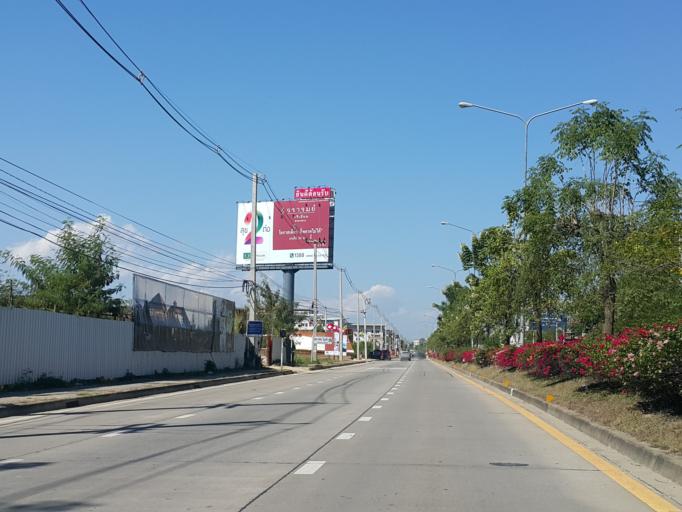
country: TH
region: Chiang Mai
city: San Sai
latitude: 18.8378
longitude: 99.0009
